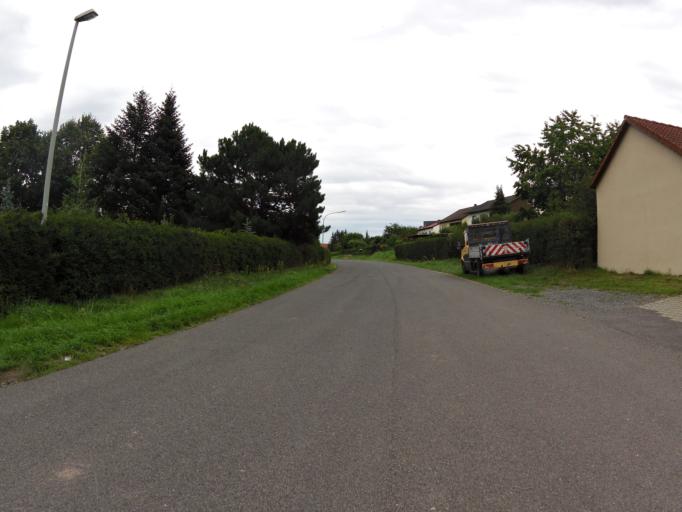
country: DE
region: Bavaria
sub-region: Regierungsbezirk Unterfranken
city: Ebelsbach
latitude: 49.9676
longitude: 10.6953
